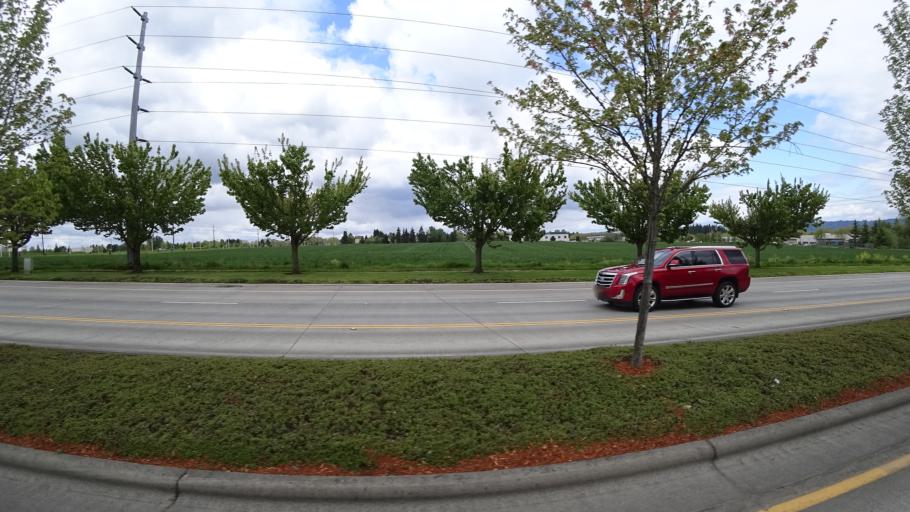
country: US
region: Oregon
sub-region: Washington County
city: Rockcreek
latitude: 45.5397
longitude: -122.8980
